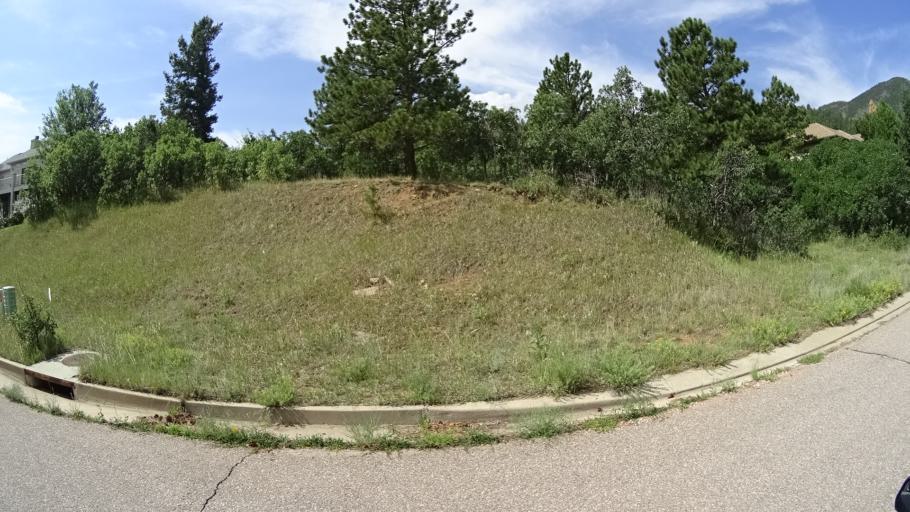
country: US
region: Colorado
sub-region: El Paso County
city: Air Force Academy
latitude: 38.9477
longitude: -104.8841
